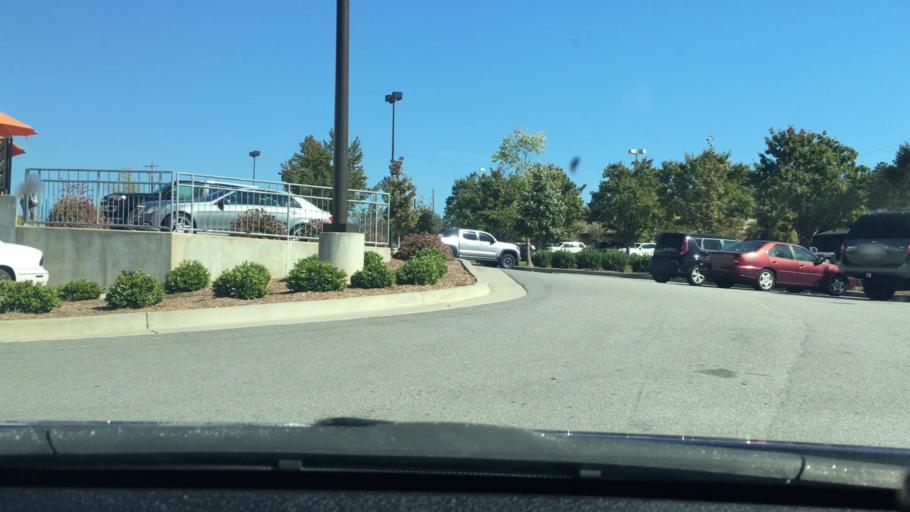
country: US
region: South Carolina
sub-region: Lexington County
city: Seven Oaks
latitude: 34.0705
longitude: -81.1538
